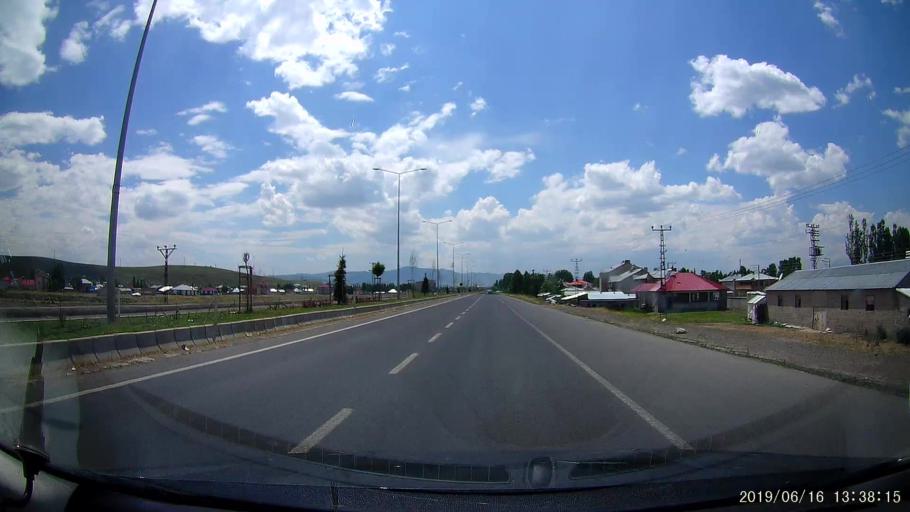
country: TR
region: Agri
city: Agri
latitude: 39.7116
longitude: 43.0765
